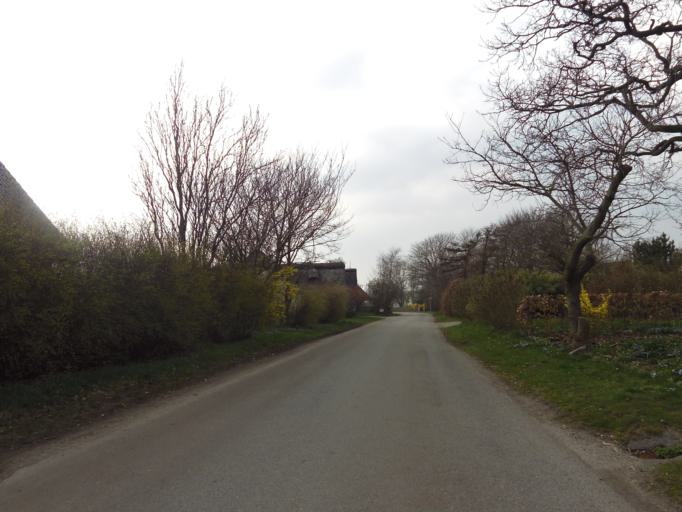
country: DK
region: South Denmark
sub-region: Esbjerg Kommune
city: Ribe
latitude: 55.3544
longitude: 8.7331
